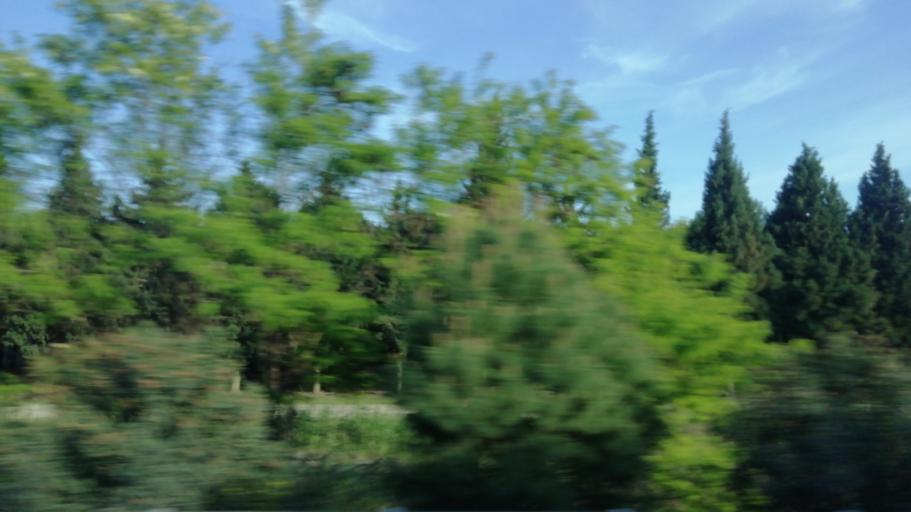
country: TR
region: Manisa
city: Saruhanli
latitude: 38.7473
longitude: 27.6161
